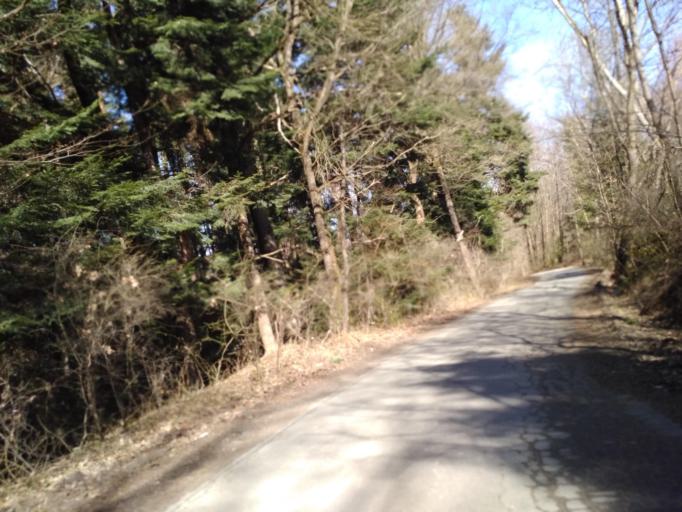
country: PL
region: Subcarpathian Voivodeship
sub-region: Powiat brzozowski
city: Orzechowka
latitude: 49.7082
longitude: 21.9661
